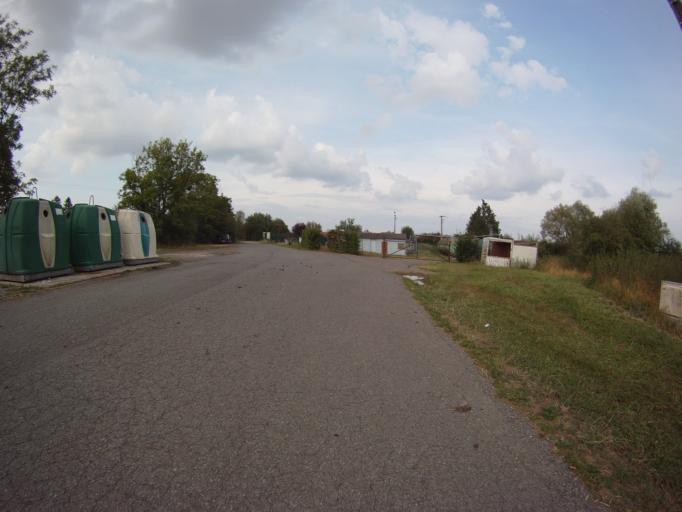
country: FR
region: Lorraine
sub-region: Departement de la Moselle
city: Mecleuves
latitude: 49.0642
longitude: 6.3124
